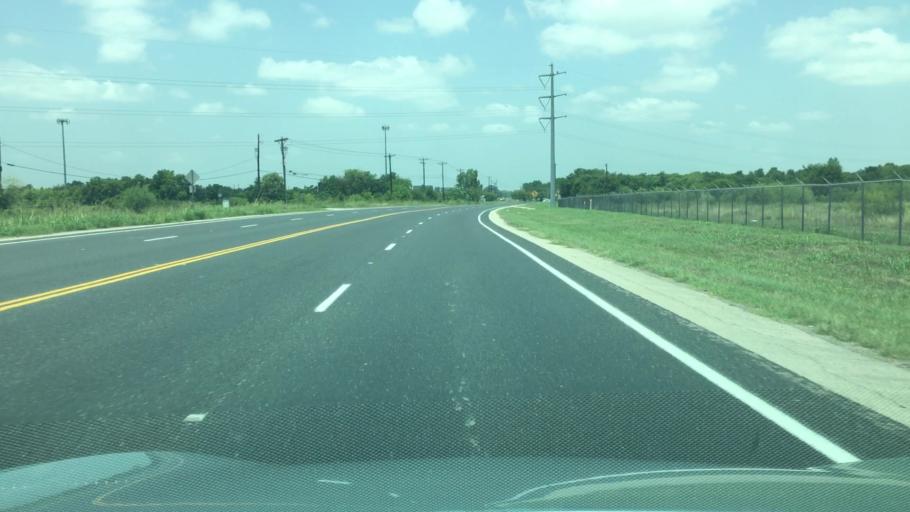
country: US
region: Texas
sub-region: Travis County
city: Austin
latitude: 30.1789
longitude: -97.6830
